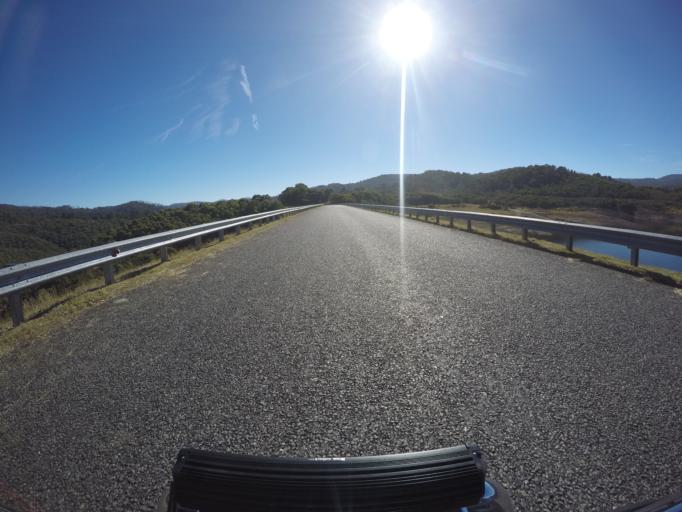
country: AU
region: New South Wales
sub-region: Snowy River
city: Jindabyne
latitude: -36.0512
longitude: 148.2745
